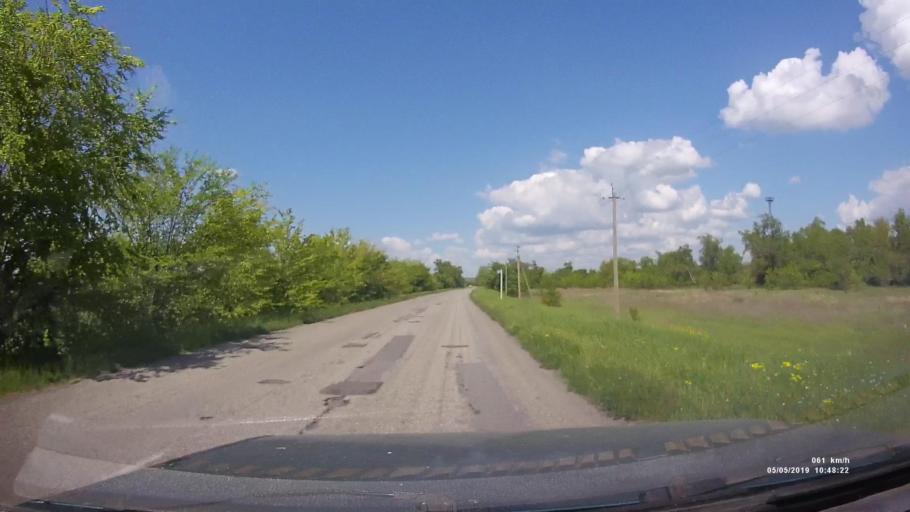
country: RU
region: Rostov
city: Ust'-Donetskiy
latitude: 47.6423
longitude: 40.8208
